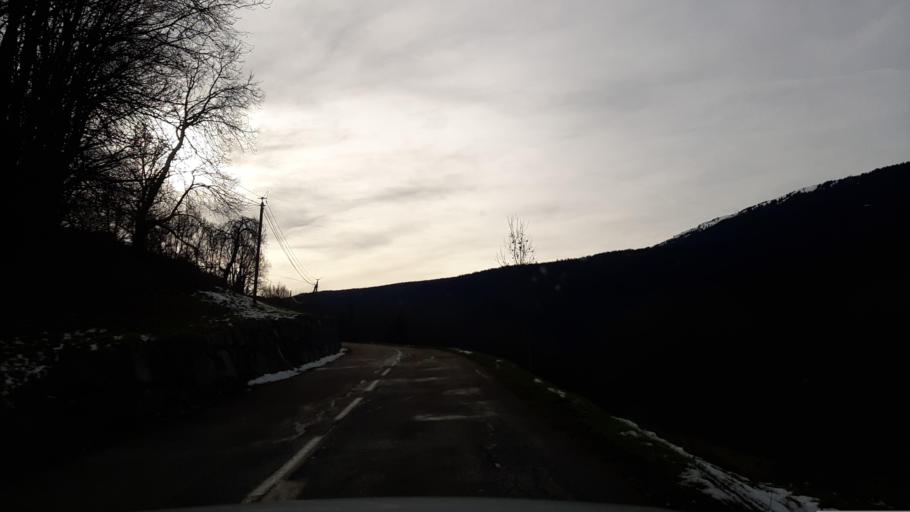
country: FR
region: Rhone-Alpes
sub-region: Departement de la Haute-Savoie
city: Cusy
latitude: 45.6618
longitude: 6.0961
